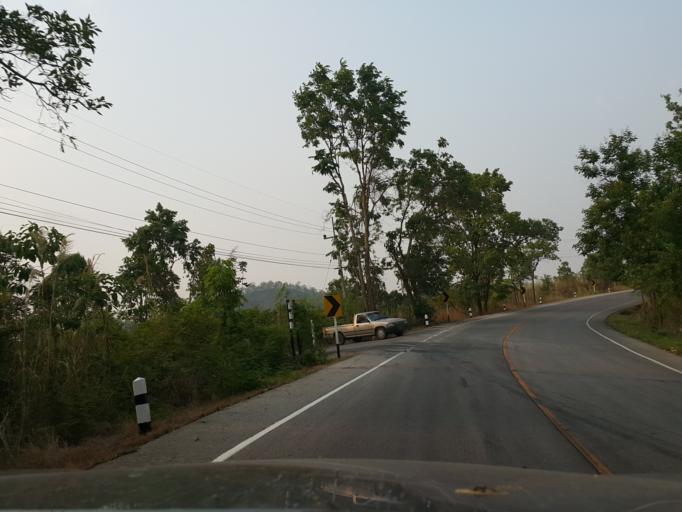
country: TH
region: Lamphun
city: Li
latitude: 17.8401
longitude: 98.9893
